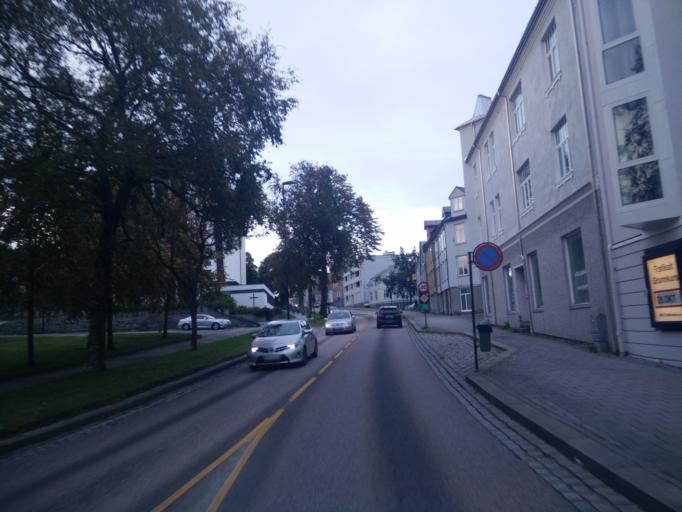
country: NO
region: More og Romsdal
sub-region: Kristiansund
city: Kristiansund
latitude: 63.1138
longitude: 7.7267
